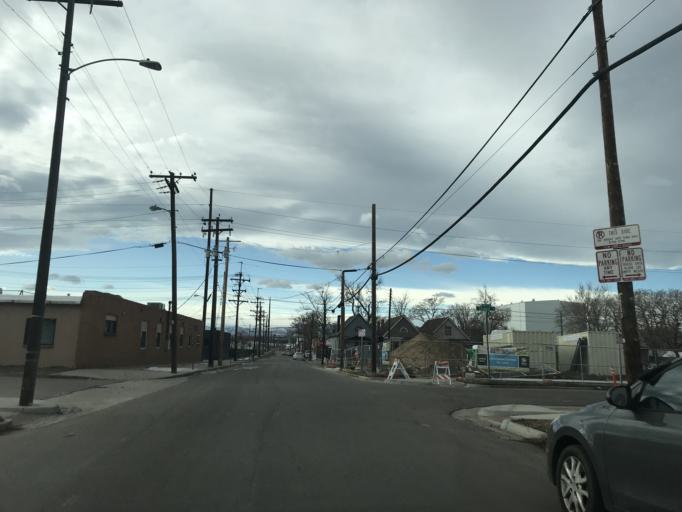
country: US
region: Colorado
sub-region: Adams County
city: Commerce City
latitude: 39.7764
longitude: -104.9563
